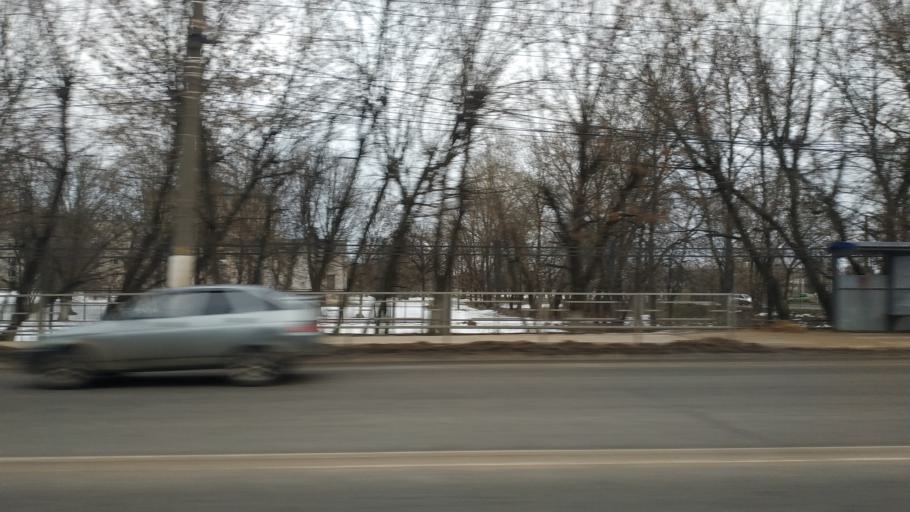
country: RU
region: Tverskaya
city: Tver
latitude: 56.8505
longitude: 35.9238
